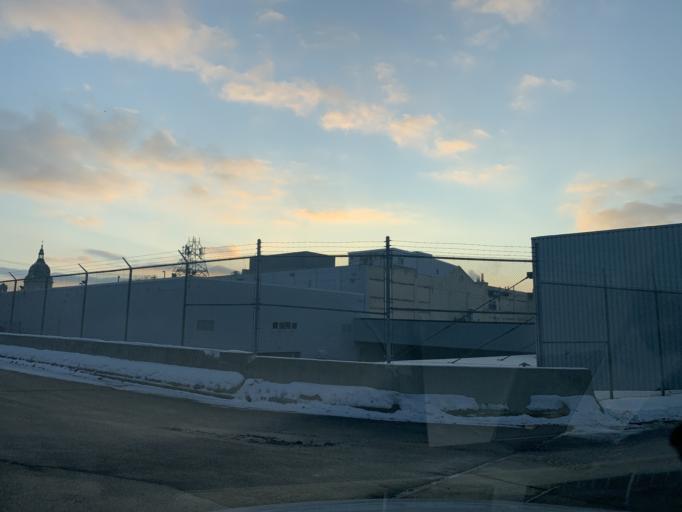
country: US
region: Minnesota
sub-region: Hennepin County
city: Minneapolis
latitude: 44.9779
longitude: -93.2839
